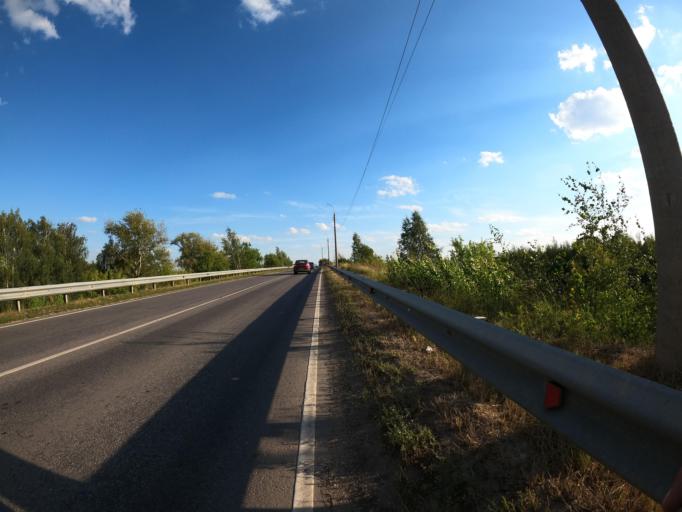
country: RU
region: Moskovskaya
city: Raduzhnyy
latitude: 55.1479
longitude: 38.7300
